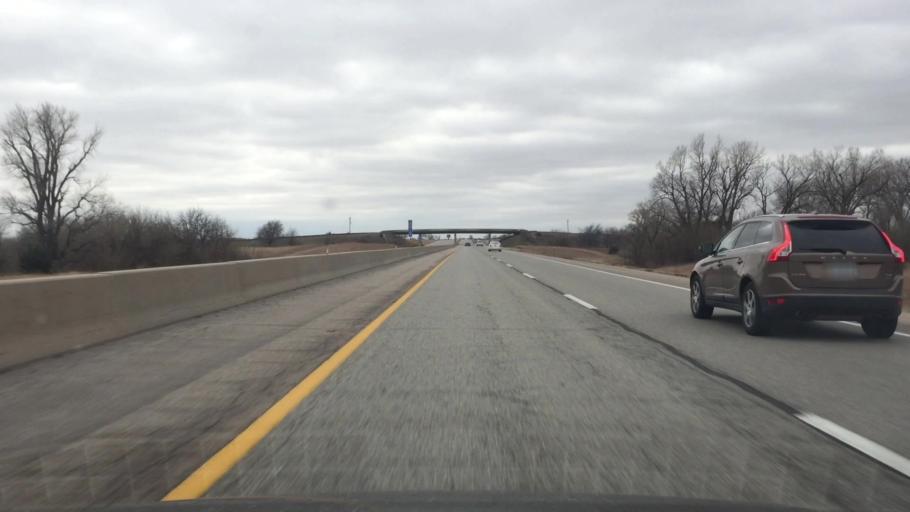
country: US
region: Kansas
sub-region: Butler County
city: El Dorado
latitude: 38.0311
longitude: -96.6573
